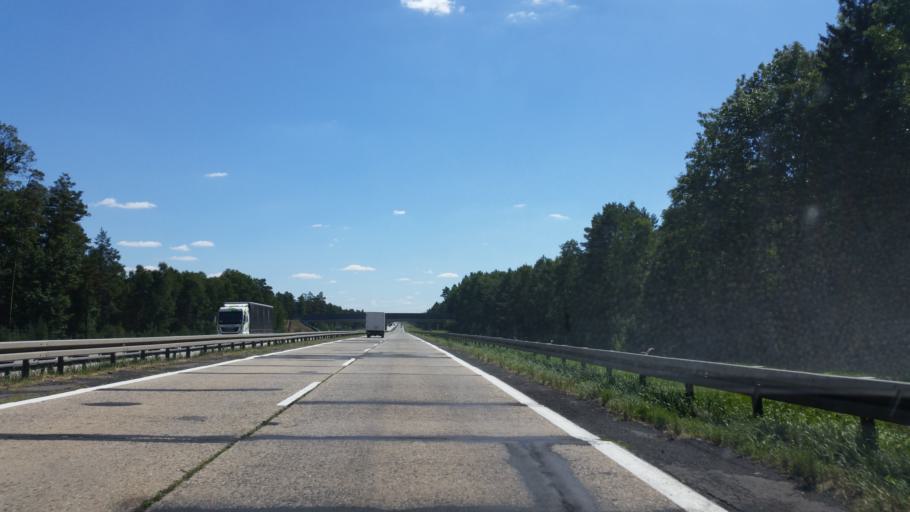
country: PL
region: Lower Silesian Voivodeship
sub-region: Powiat boleslawiecki
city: Boleslawiec
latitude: 51.3932
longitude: 15.5313
